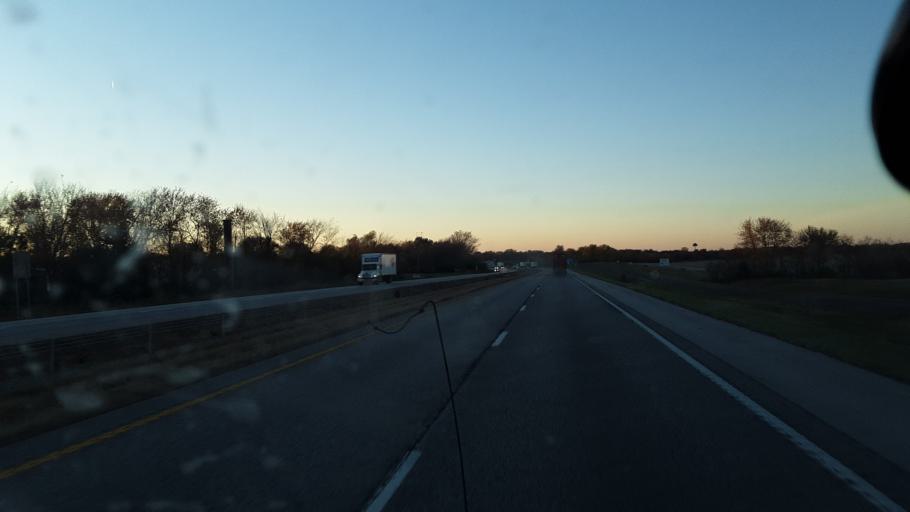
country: US
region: Missouri
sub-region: Warren County
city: Warrenton
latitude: 38.8540
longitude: -91.2938
